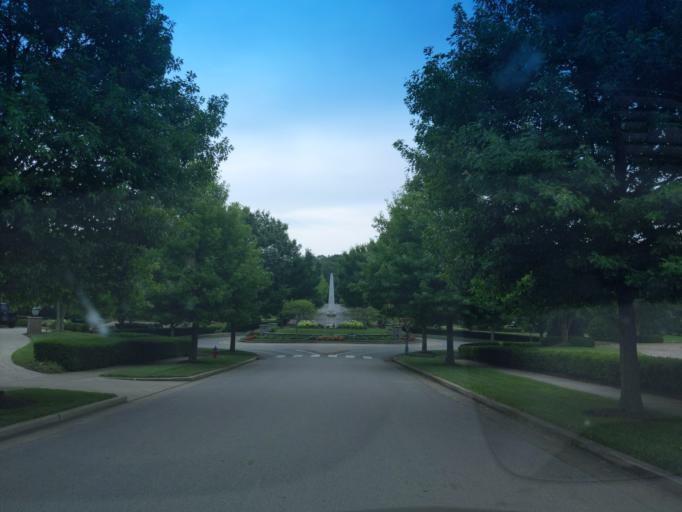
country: US
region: Tennessee
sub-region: Williamson County
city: Brentwood Estates
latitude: 36.0273
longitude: -86.7702
